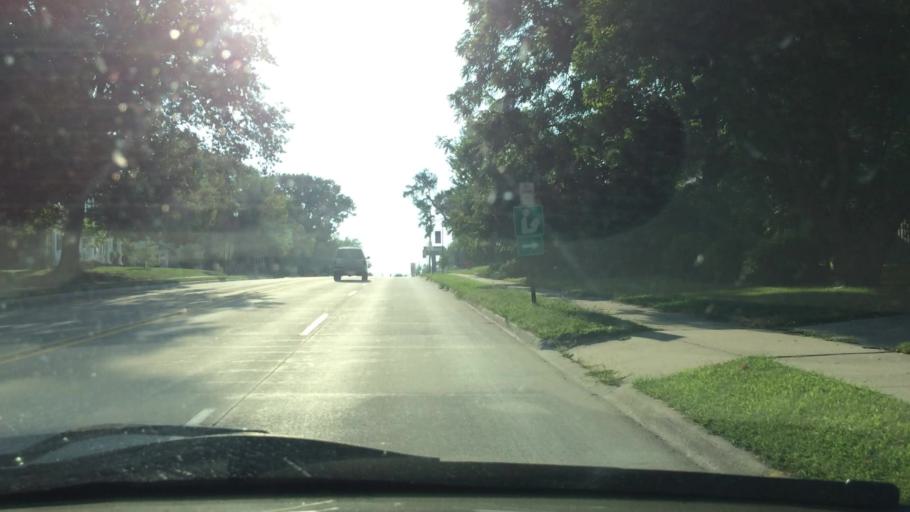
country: US
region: Iowa
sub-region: Henry County
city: Mount Pleasant
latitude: 40.9650
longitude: -91.5482
